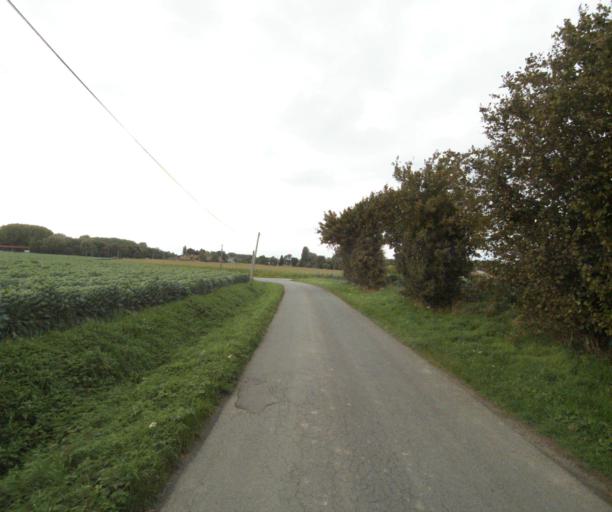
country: FR
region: Nord-Pas-de-Calais
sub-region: Departement du Nord
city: Ennetieres-en-Weppes
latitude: 50.6358
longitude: 2.9496
